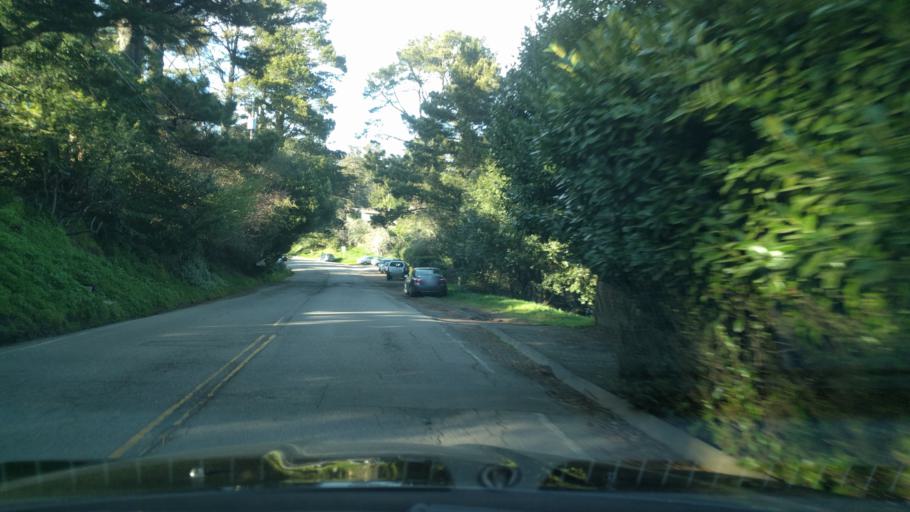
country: US
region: California
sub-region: Alameda County
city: Piedmont
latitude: 37.8225
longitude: -122.1871
